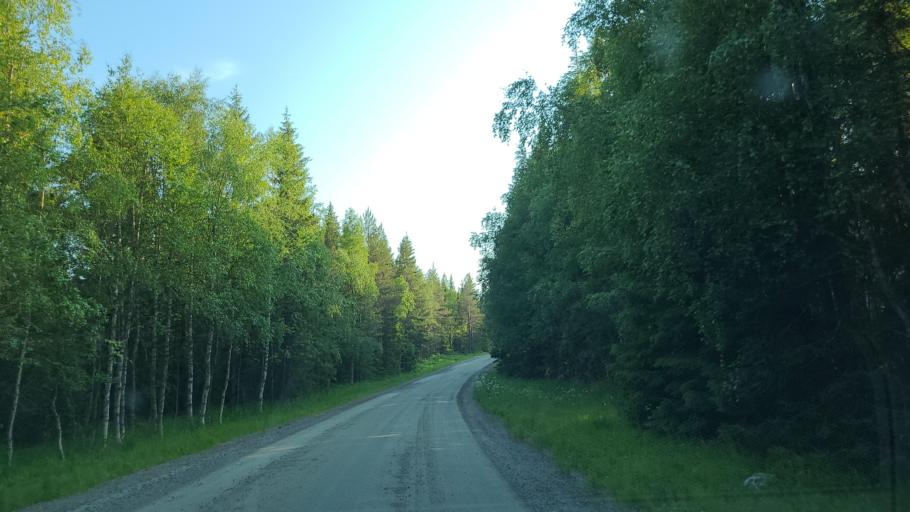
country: SE
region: Vaesterbotten
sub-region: Skelleftea Kommun
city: Burea
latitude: 64.3647
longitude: 21.4525
